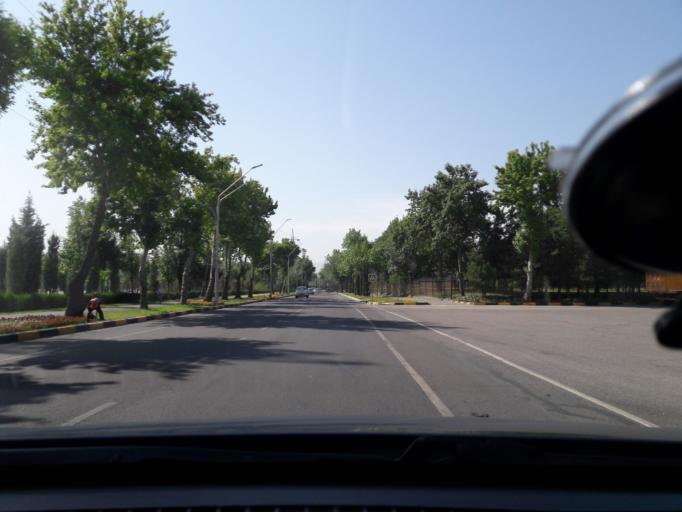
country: TJ
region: Dushanbe
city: Dushanbe
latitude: 38.5902
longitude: 68.7678
